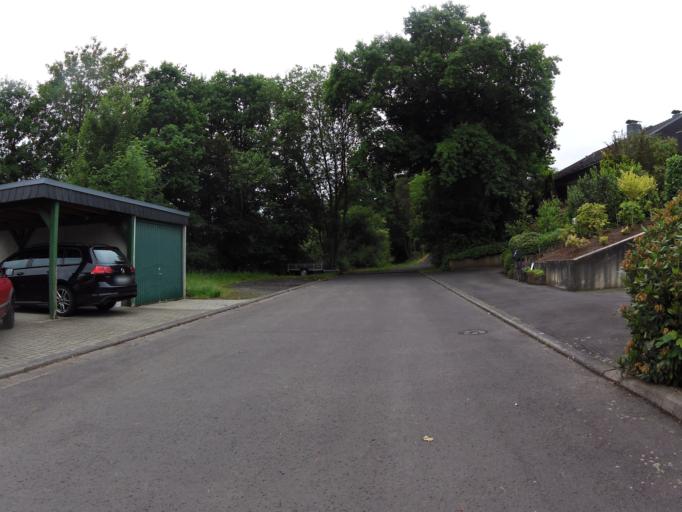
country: DE
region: Hesse
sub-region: Regierungsbezirk Kassel
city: Bad Hersfeld
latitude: 50.8672
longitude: 9.6826
